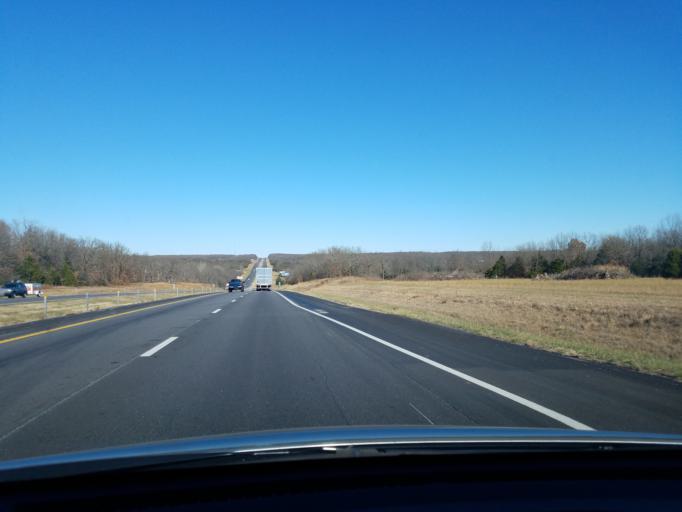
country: US
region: Missouri
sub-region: Webster County
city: Marshfield
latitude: 37.4315
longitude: -92.8786
